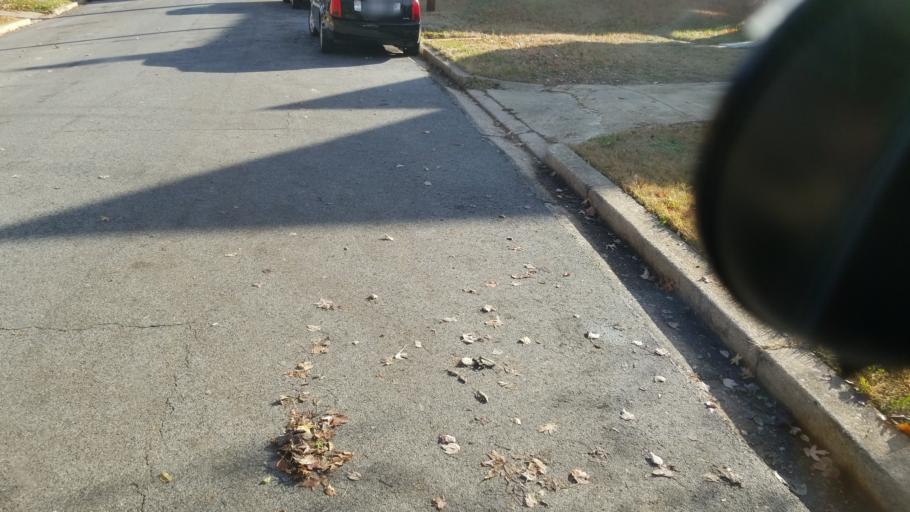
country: US
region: Maryland
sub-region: Prince George's County
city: Silver Hill
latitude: 38.8605
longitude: -76.9553
